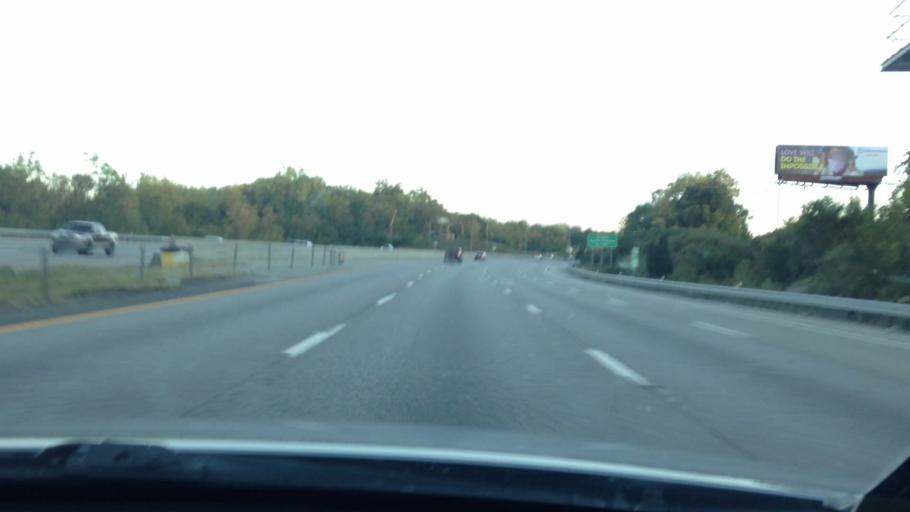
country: US
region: Missouri
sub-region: Jackson County
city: Sugar Creek
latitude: 39.0729
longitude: -94.4886
